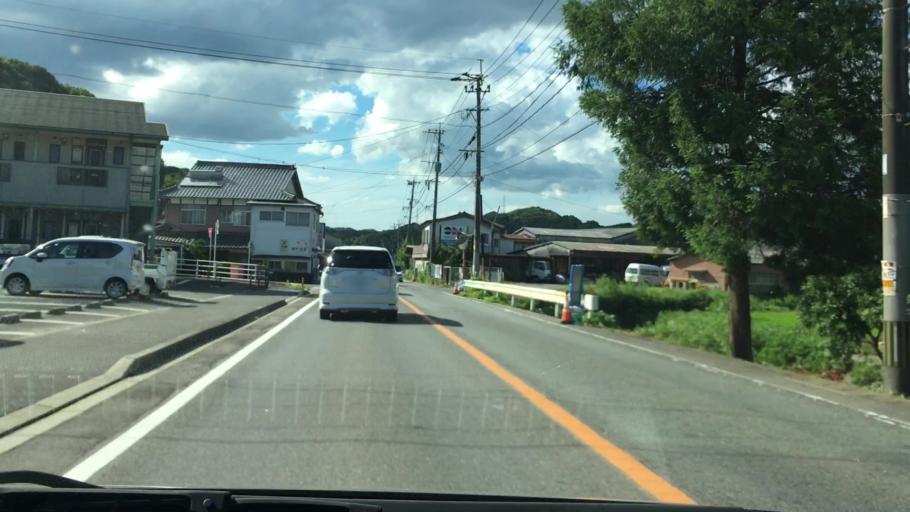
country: JP
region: Saga Prefecture
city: Takeocho-takeo
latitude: 33.1912
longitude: 129.9829
